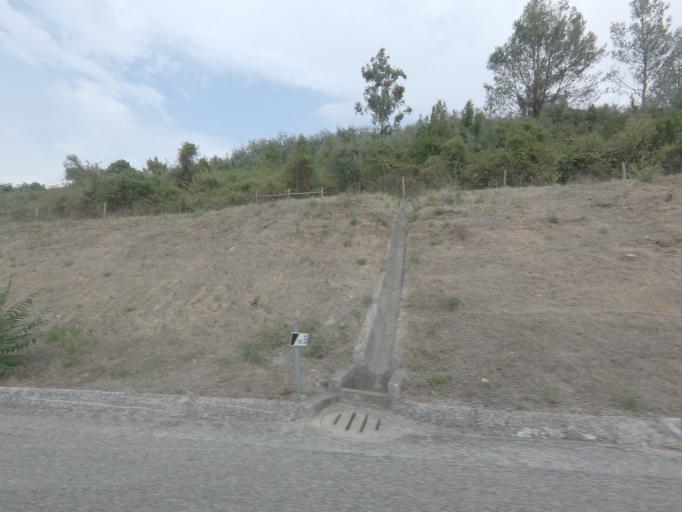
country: PT
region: Coimbra
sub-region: Coimbra
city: Coimbra
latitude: 40.2111
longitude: -8.4461
